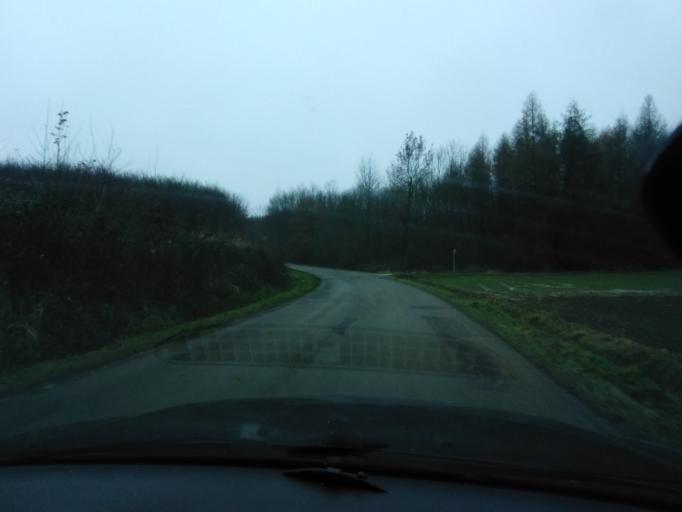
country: PL
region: Subcarpathian Voivodeship
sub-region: Powiat przeworski
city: Zurawiczki
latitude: 49.9985
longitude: 22.5135
